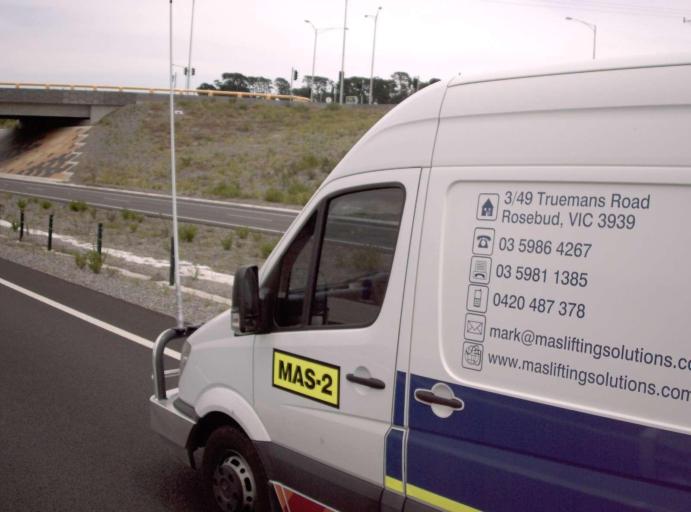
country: AU
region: Victoria
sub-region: Frankston
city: Langwarrin
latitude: -38.1806
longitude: 145.1598
